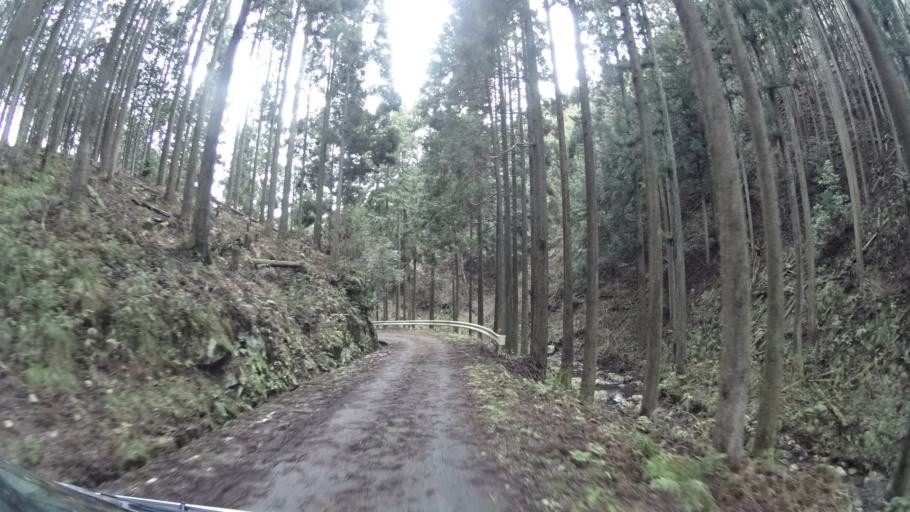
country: JP
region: Kyoto
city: Ayabe
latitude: 35.3167
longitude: 135.3655
